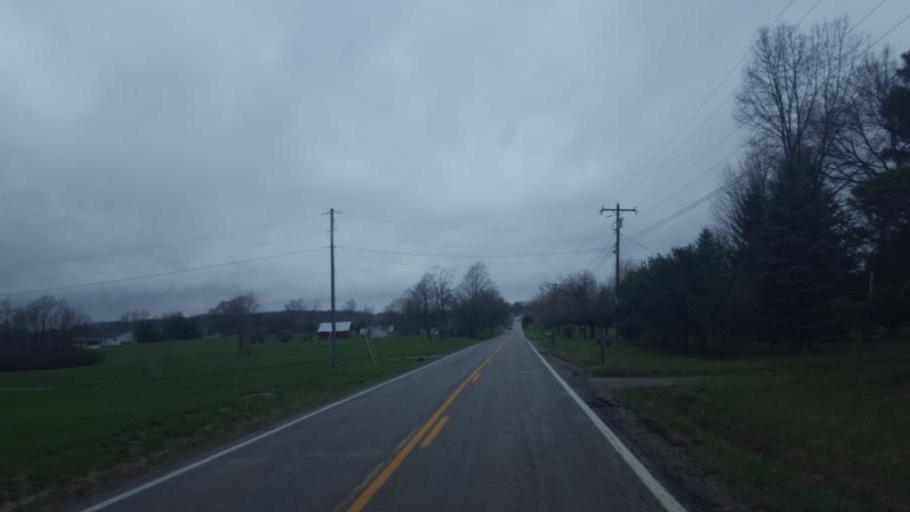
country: US
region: Ohio
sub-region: Morrow County
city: Cardington
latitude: 40.4822
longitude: -82.8356
